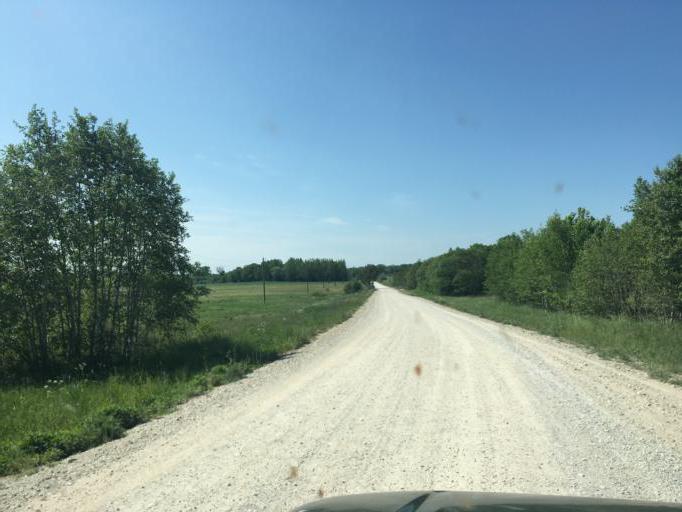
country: LV
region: Talsu Rajons
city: Valdemarpils
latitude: 57.4471
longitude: 22.5569
